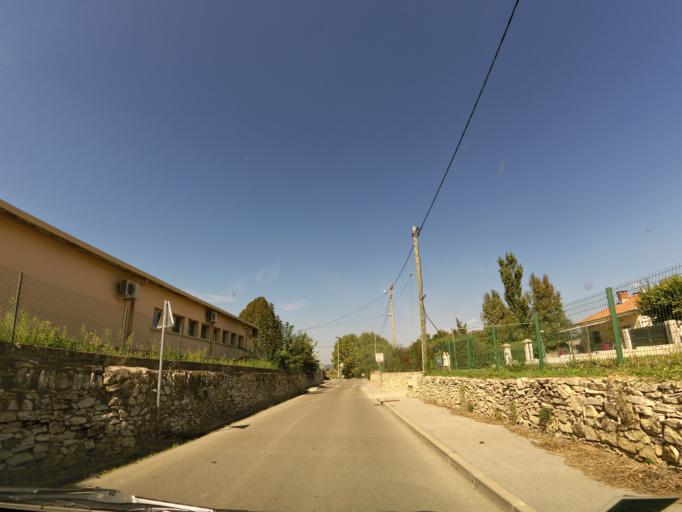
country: FR
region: Languedoc-Roussillon
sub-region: Departement du Gard
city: Nages-et-Solorgues
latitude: 43.7758
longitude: 4.2350
